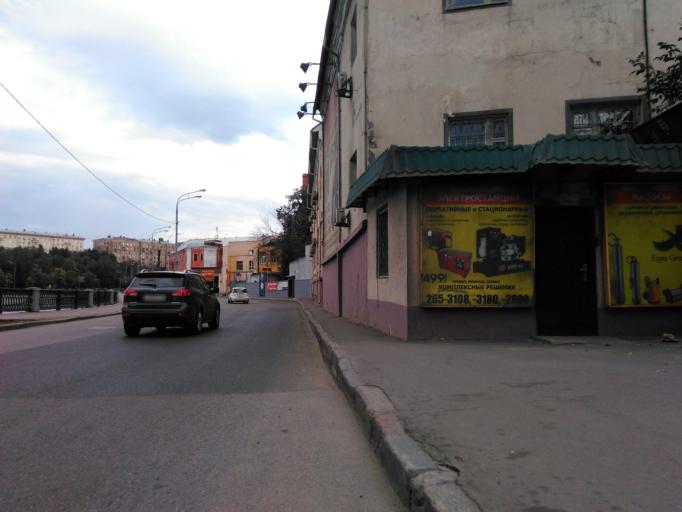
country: RU
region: Moscow
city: Lefortovo
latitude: 55.7818
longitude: 37.6991
